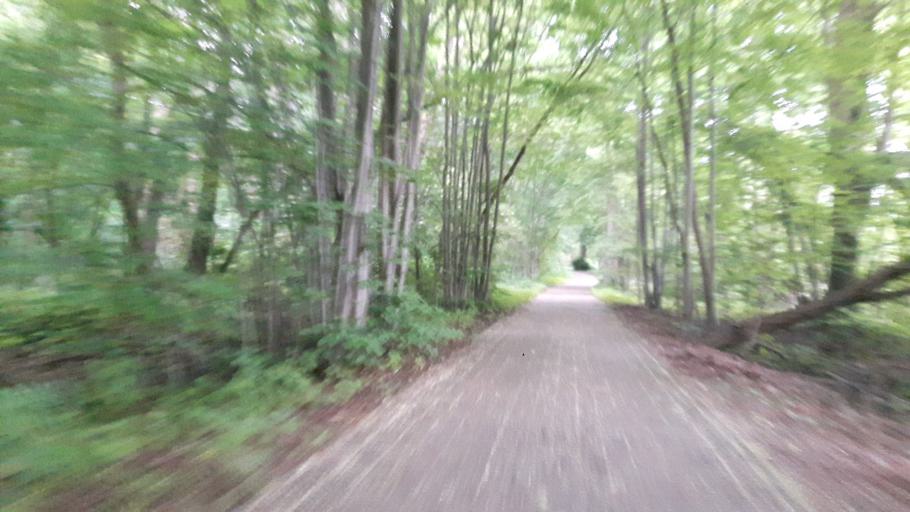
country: DE
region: Brandenburg
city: Gartz
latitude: 53.2271
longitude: 14.4116
